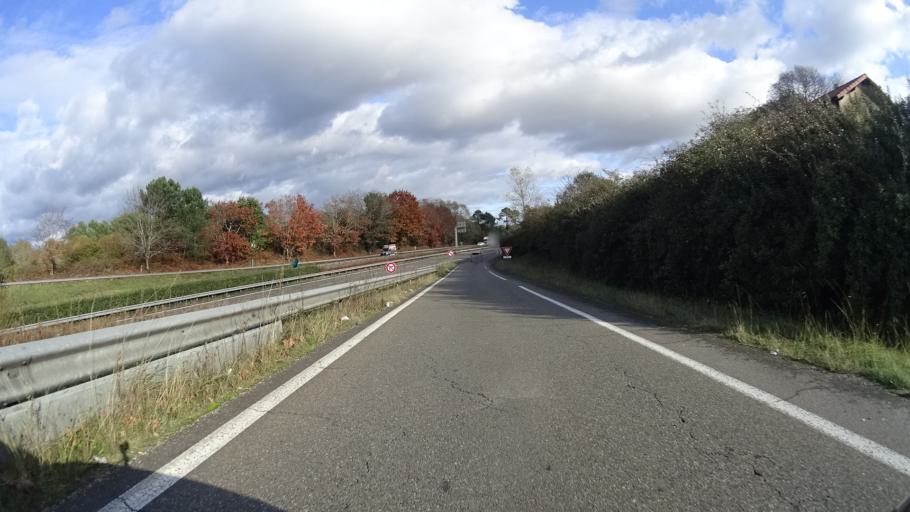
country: FR
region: Aquitaine
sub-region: Departement des Landes
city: Saint-Paul-les-Dax
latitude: 43.7444
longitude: -1.0544
